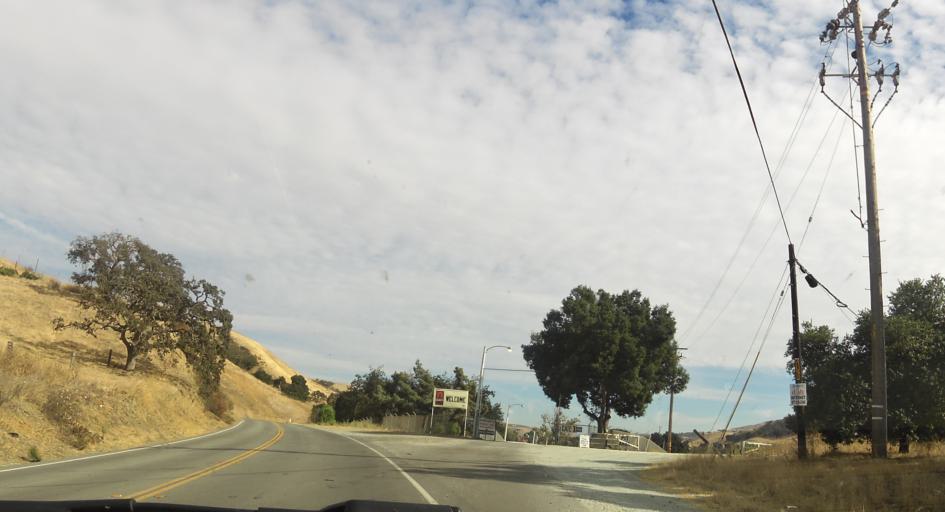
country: US
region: California
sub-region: San Benito County
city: Ridgemark
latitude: 36.7718
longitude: -121.3079
